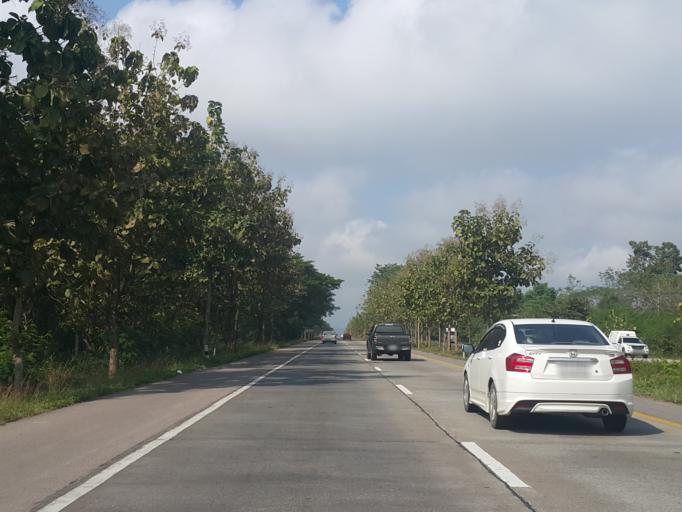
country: TH
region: Lampang
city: Hang Chat
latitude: 18.3201
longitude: 99.3069
